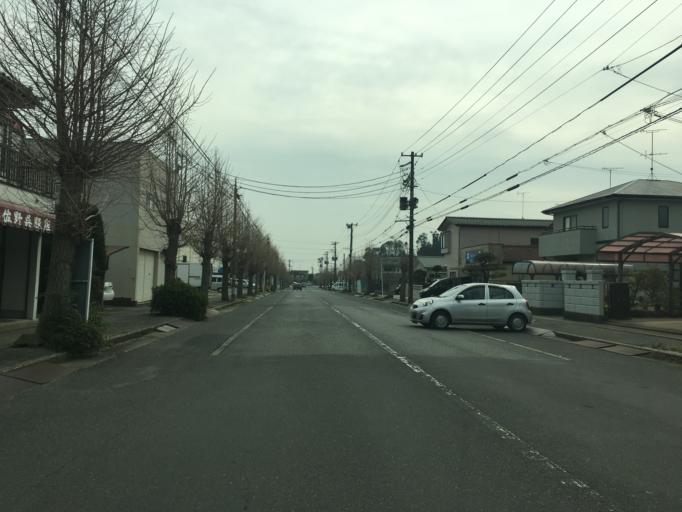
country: JP
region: Fukushima
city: Iwaki
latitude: 36.9823
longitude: 140.8867
